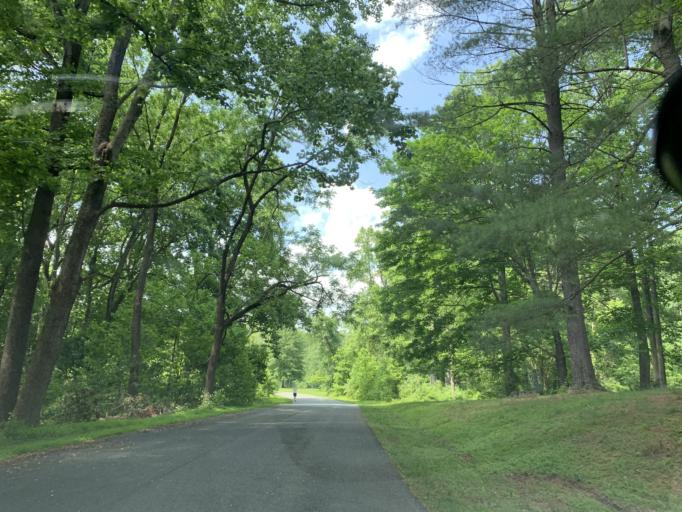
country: US
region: Maryland
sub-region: Carroll County
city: Eldersburg
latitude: 39.3586
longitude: -76.8854
